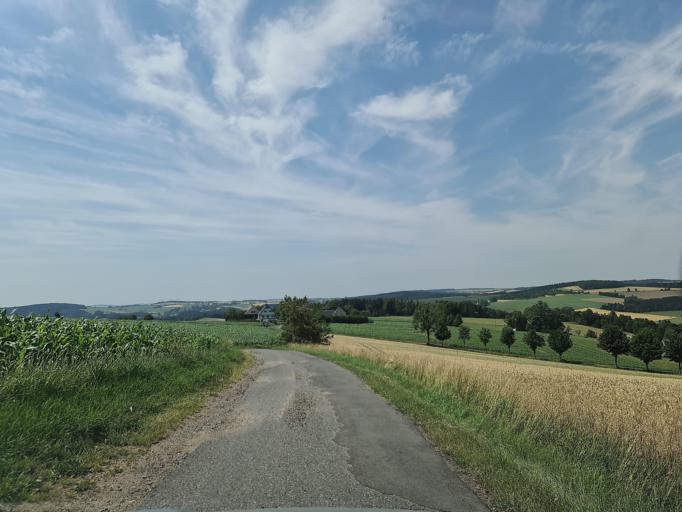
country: DE
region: Saxony
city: Neuhausen
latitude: 50.6630
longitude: 13.4666
